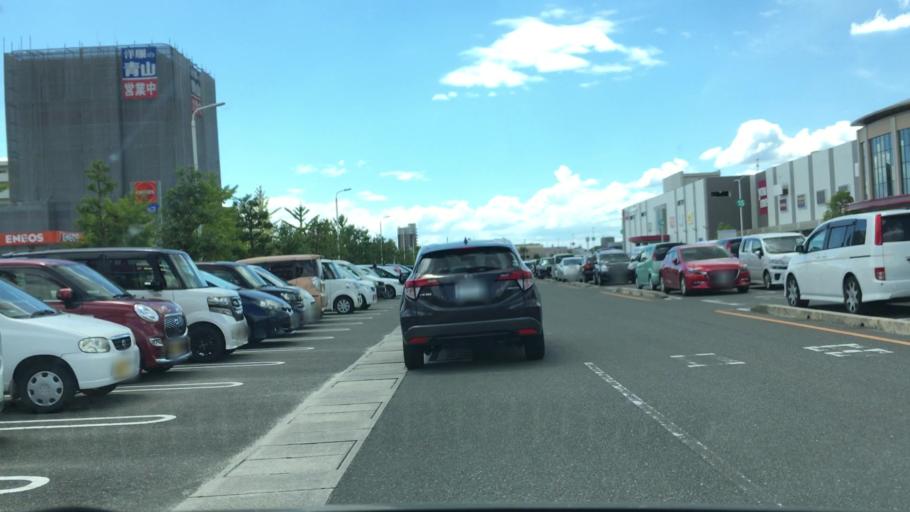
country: JP
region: Saga Prefecture
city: Saga-shi
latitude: 33.2748
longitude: 130.3097
